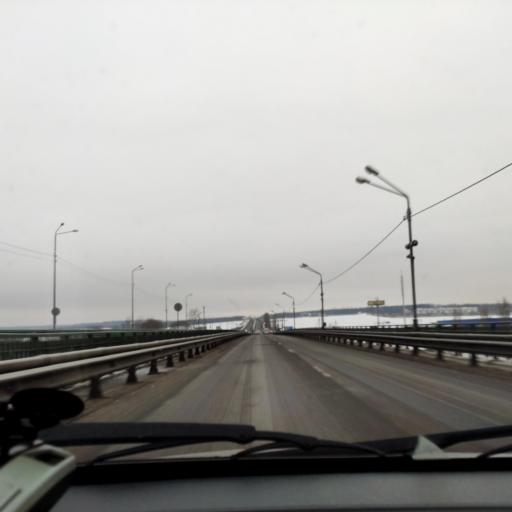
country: RU
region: Voronezj
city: Pridonskoy
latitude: 51.6512
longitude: 39.0690
